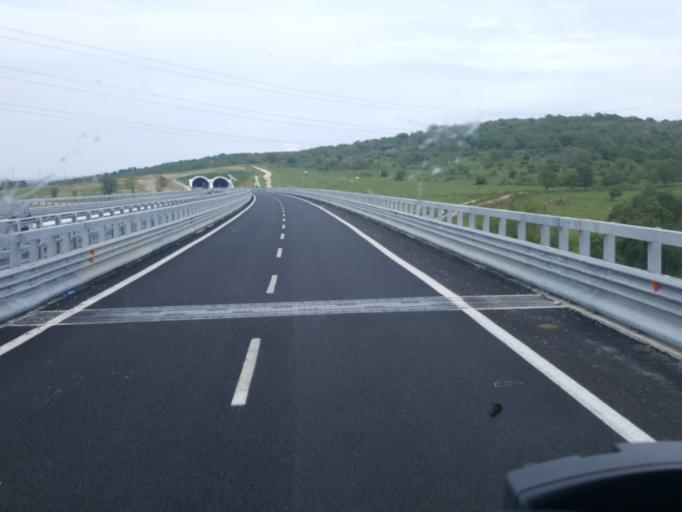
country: IT
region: Latium
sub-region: Provincia di Viterbo
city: Monte Romano
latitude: 42.2820
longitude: 11.9273
